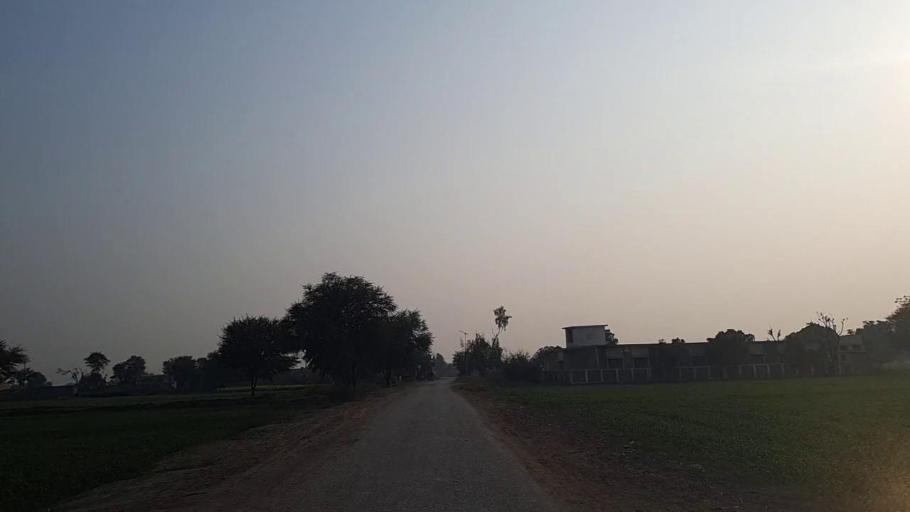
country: PK
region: Sindh
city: Nawabshah
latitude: 26.2163
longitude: 68.4730
